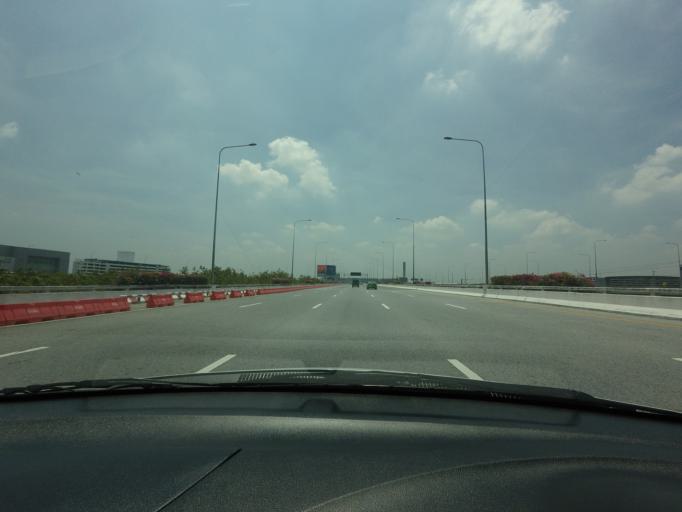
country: TH
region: Bangkok
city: Lat Krabang
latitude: 13.7103
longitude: 100.7558
